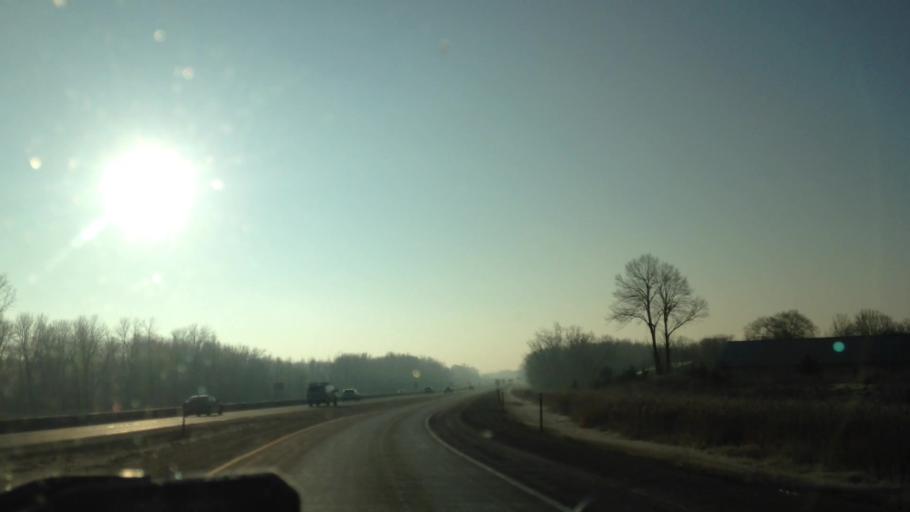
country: US
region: Wisconsin
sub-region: Washington County
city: Slinger
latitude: 43.4214
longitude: -88.3359
